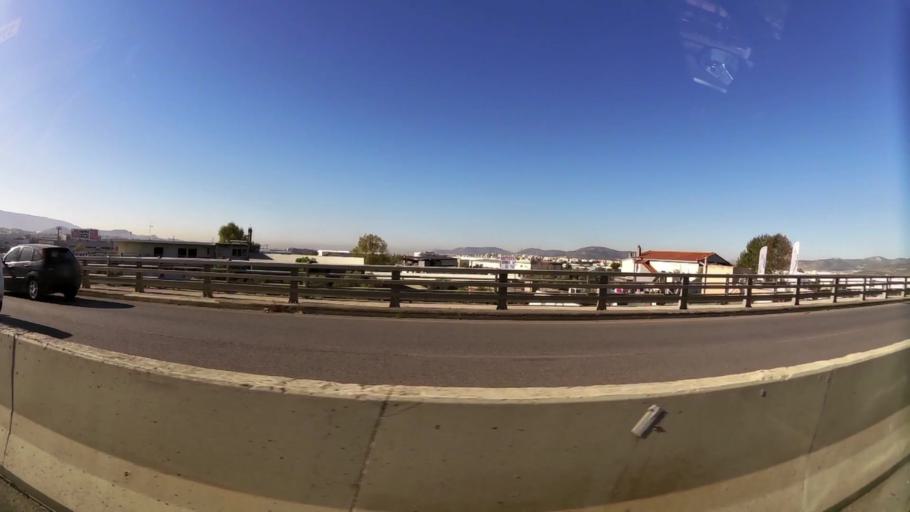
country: GR
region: Attica
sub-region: Nomarchia Athinas
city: Metamorfosi
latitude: 38.0870
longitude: 23.7623
